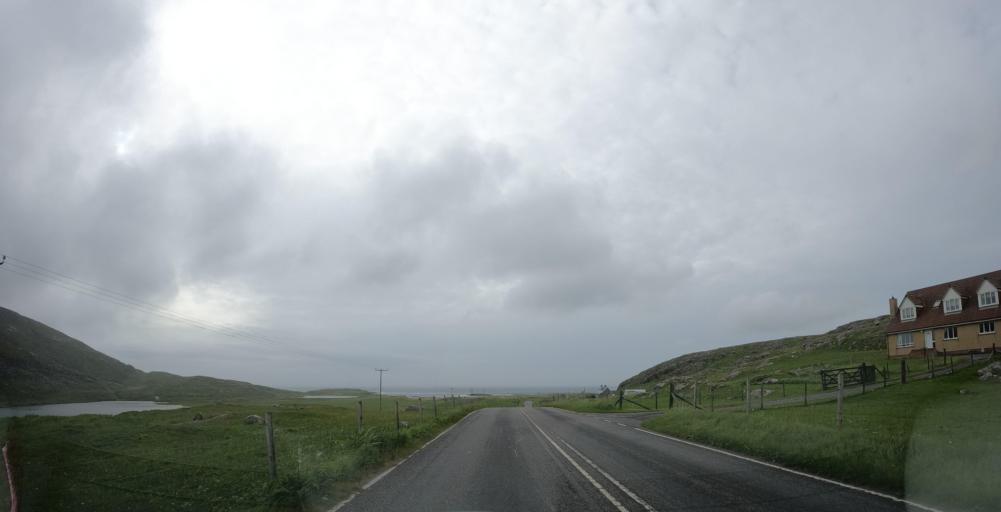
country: GB
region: Scotland
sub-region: Eilean Siar
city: Barra
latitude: 56.9664
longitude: -7.5138
